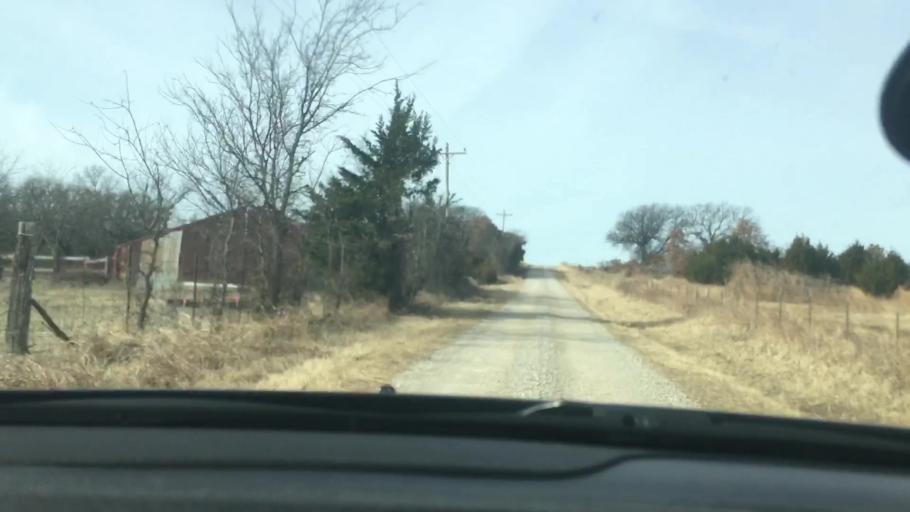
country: US
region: Oklahoma
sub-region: Garvin County
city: Wynnewood
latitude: 34.6374
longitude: -97.2405
